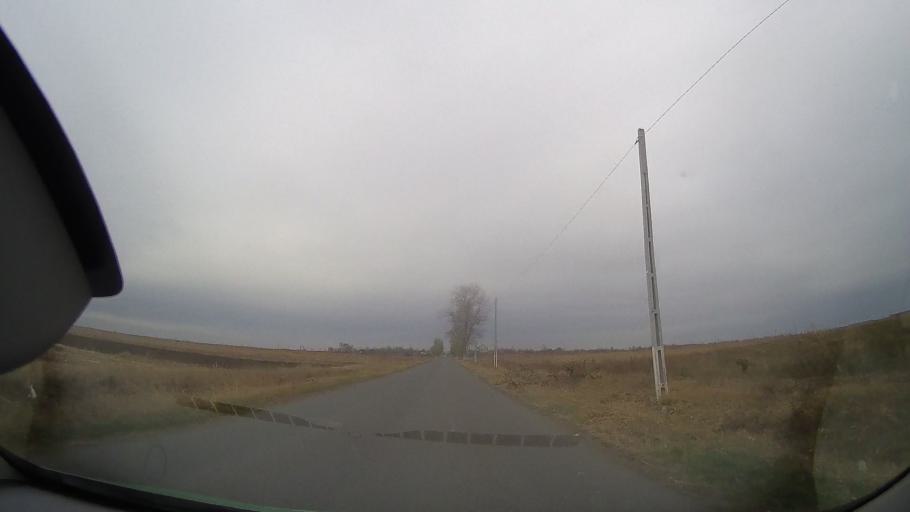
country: RO
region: Braila
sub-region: Comuna Budesti
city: Tataru
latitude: 44.8704
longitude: 27.4285
